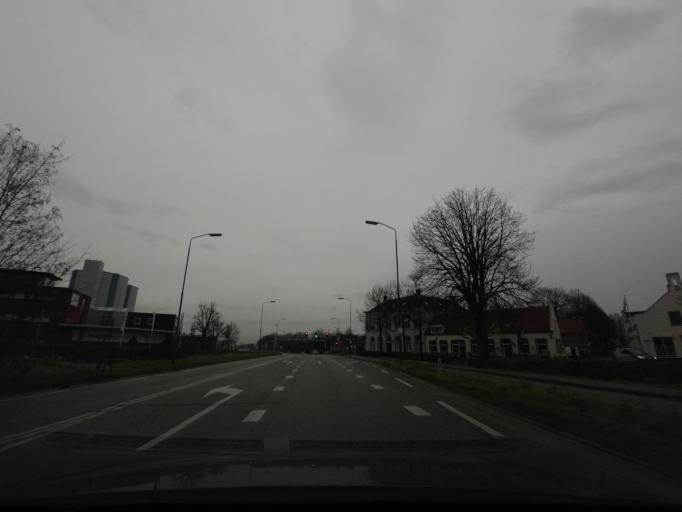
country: NL
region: North Brabant
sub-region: Gemeente Moerdijk
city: Klundert
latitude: 51.6470
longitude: 4.6091
